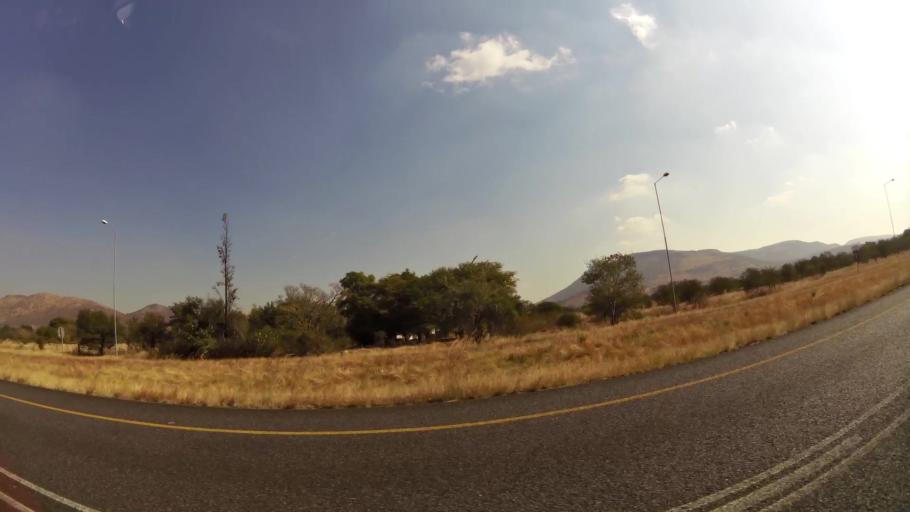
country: ZA
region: North-West
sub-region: Bojanala Platinum District Municipality
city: Rustenburg
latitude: -25.6177
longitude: 27.1549
